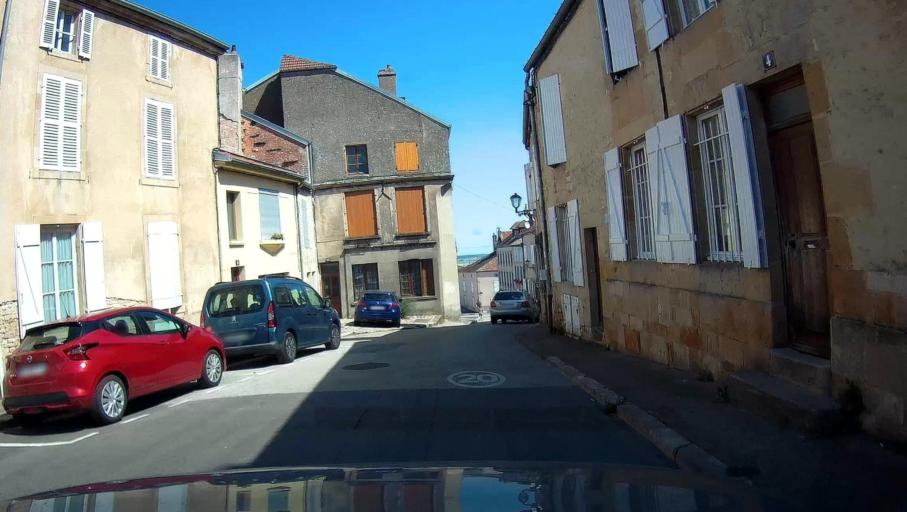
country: FR
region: Champagne-Ardenne
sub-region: Departement de la Haute-Marne
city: Langres
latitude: 47.8669
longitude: 5.3353
